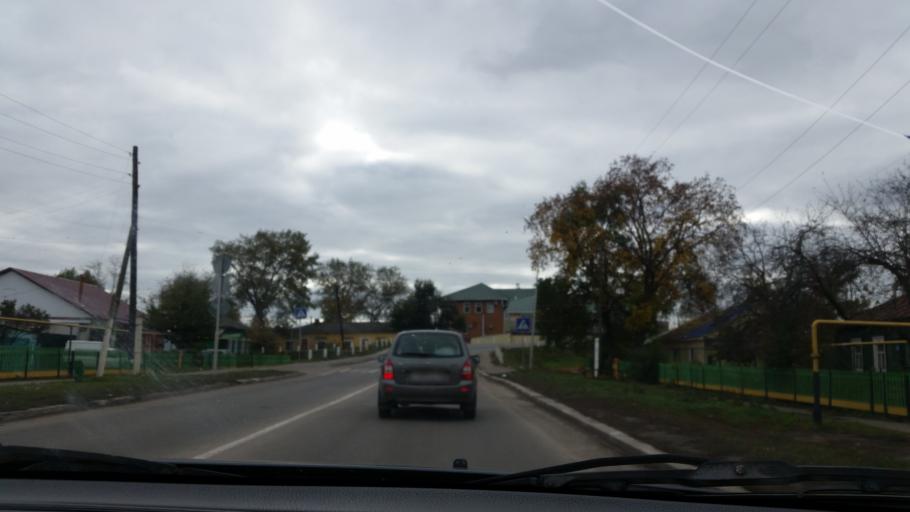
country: RU
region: Lipetsk
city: Gryazi
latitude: 52.4880
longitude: 39.9492
